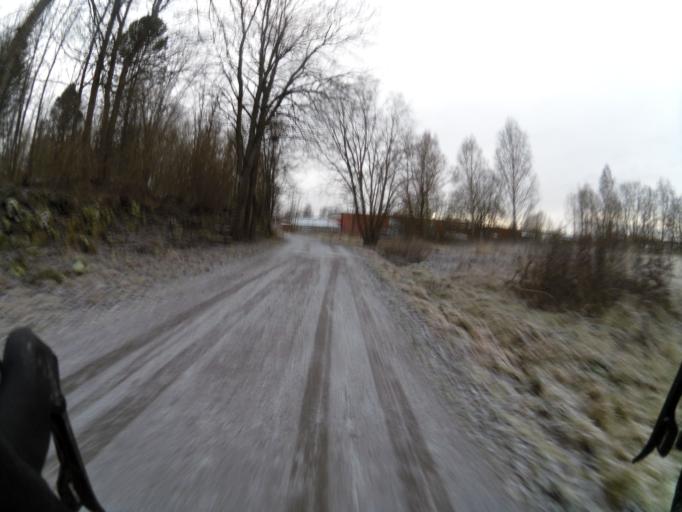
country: SE
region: Gaevleborg
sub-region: Gavle Kommun
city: Gavle
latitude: 60.6736
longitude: 17.1859
